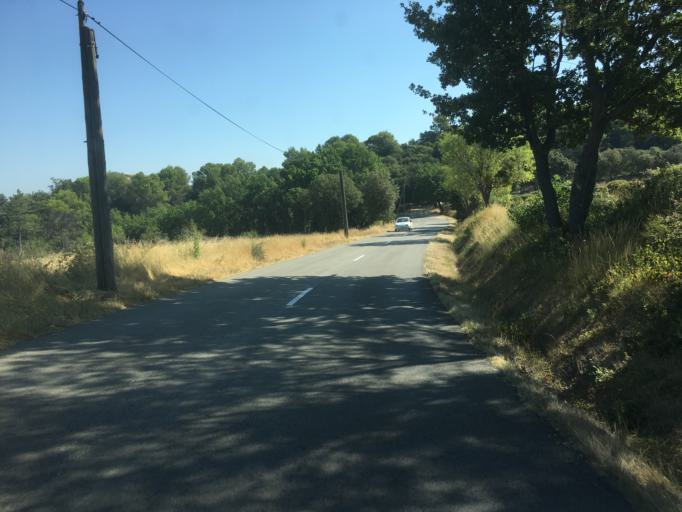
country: FR
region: Provence-Alpes-Cote d'Azur
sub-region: Departement des Alpes-de-Haute-Provence
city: Volx
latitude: 43.8346
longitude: 5.8662
